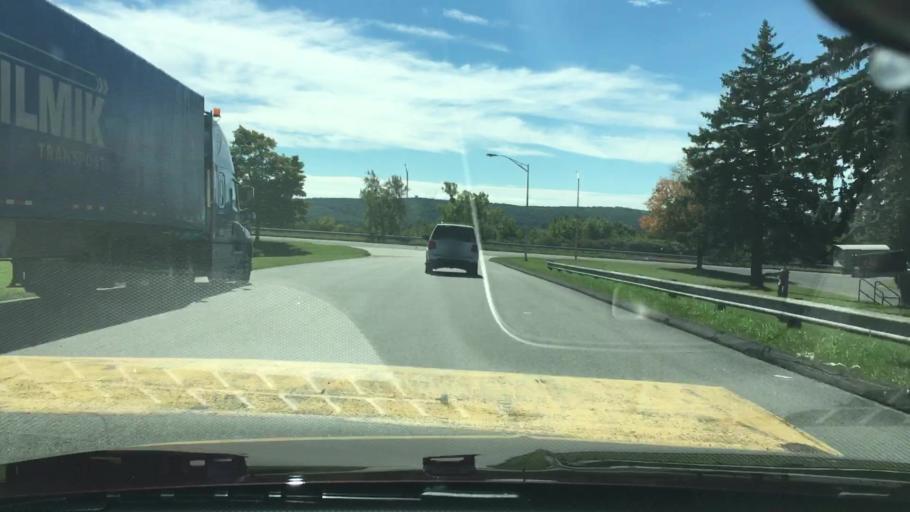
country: US
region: Connecticut
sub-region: Litchfield County
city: Terryville
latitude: 41.6931
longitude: -72.9818
